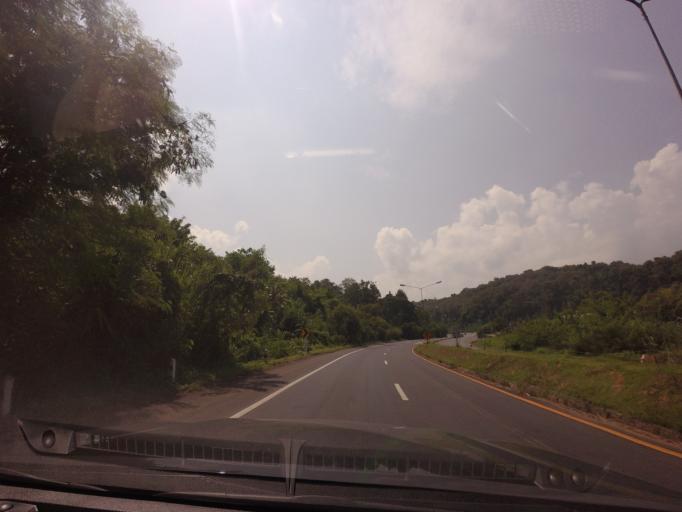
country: TH
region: Phrae
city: Den Chai
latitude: 17.8803
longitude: 100.0464
